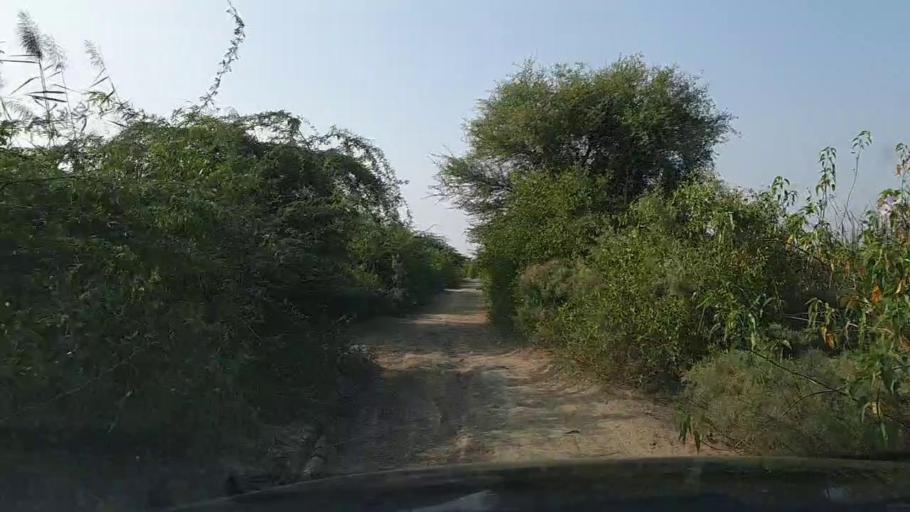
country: PK
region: Sindh
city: Mirpur Batoro
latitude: 24.6474
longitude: 68.2789
